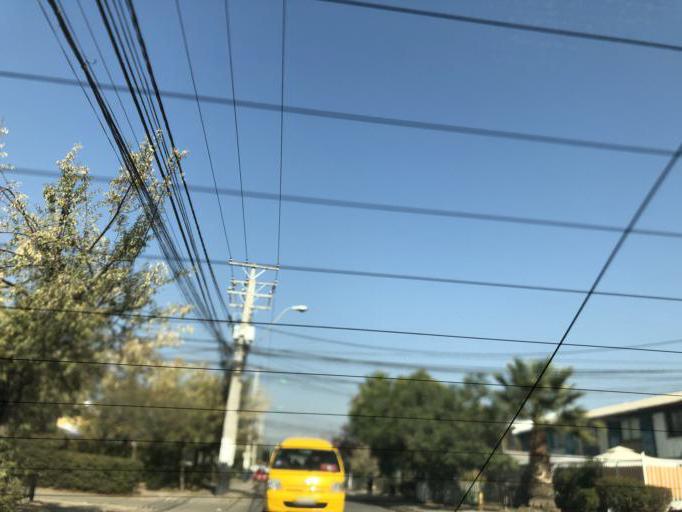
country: CL
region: Santiago Metropolitan
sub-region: Provincia de Cordillera
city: Puente Alto
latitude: -33.5997
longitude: -70.5585
